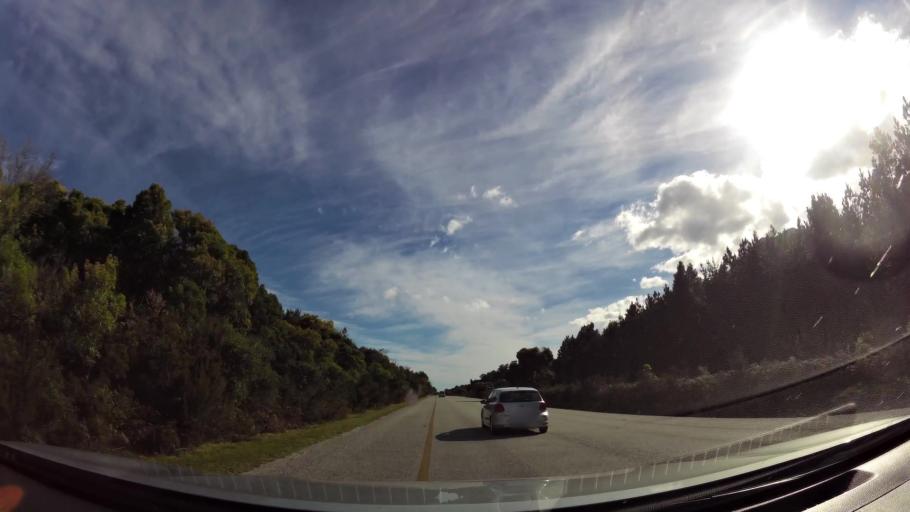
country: ZA
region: Eastern Cape
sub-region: Cacadu District Municipality
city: Kareedouw
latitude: -33.9912
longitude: 24.1195
